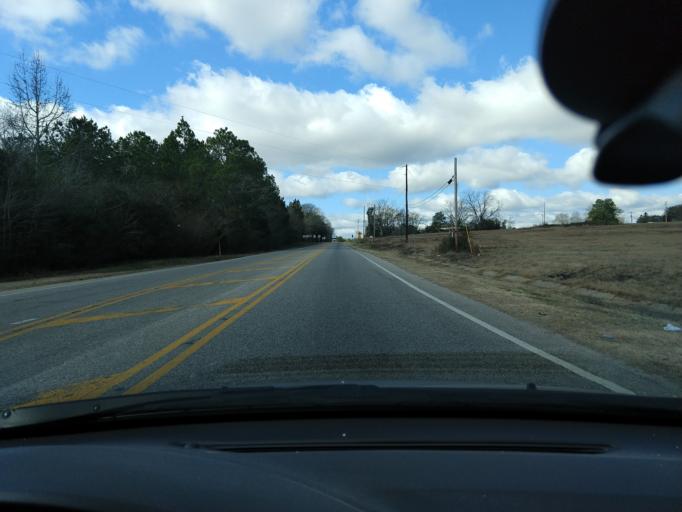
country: US
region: Alabama
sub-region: Coffee County
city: Enterprise
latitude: 31.3242
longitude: -85.8904
